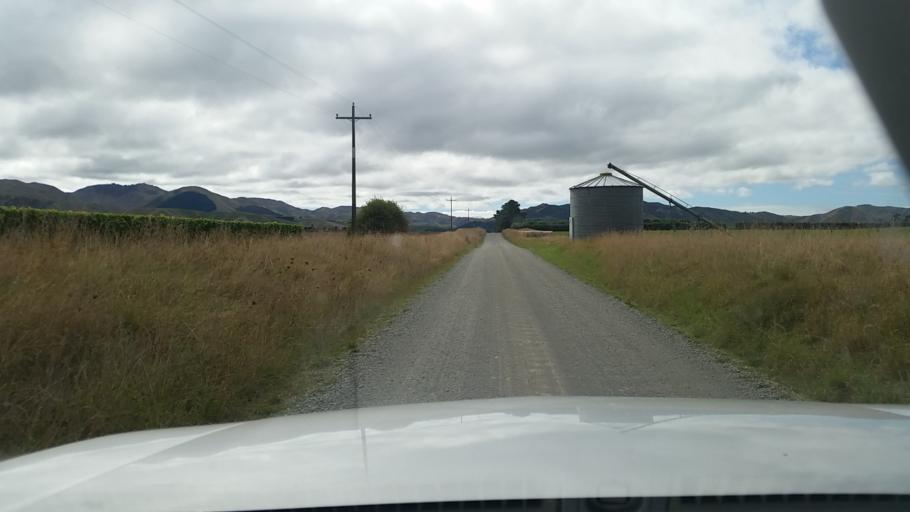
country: NZ
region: Marlborough
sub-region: Marlborough District
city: Blenheim
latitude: -41.6806
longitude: 174.0387
